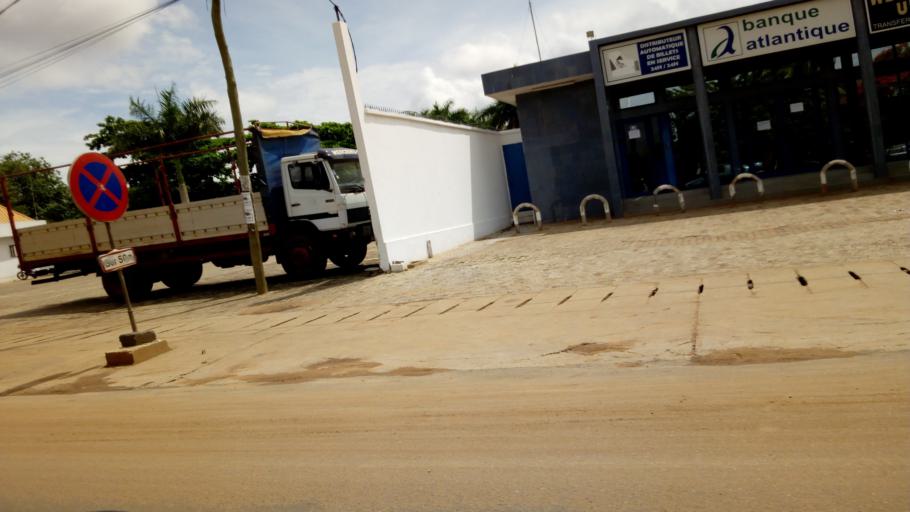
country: TG
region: Maritime
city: Lome
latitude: 6.2342
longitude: 1.2105
